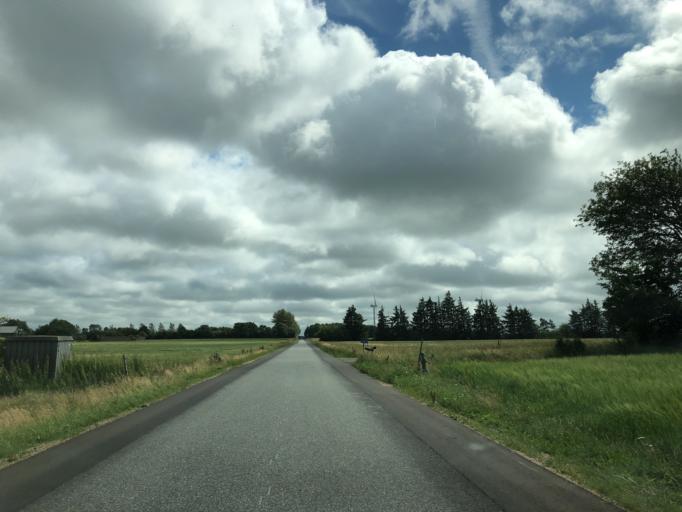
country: DK
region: Central Jutland
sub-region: Holstebro Kommune
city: Holstebro
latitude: 56.3317
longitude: 8.4707
